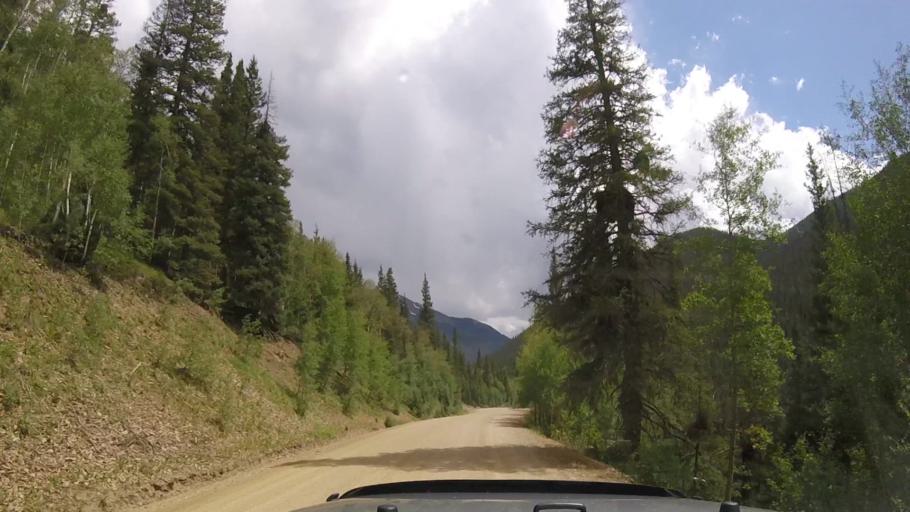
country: US
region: Colorado
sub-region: San Juan County
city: Silverton
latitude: 37.8317
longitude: -107.6712
